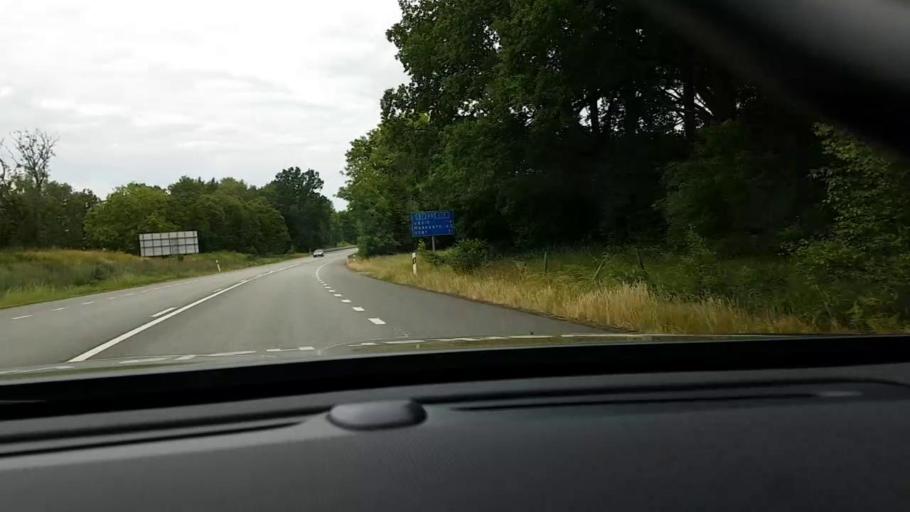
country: SE
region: Skane
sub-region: Hassleholms Kommun
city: Hassleholm
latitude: 56.1443
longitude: 13.8037
